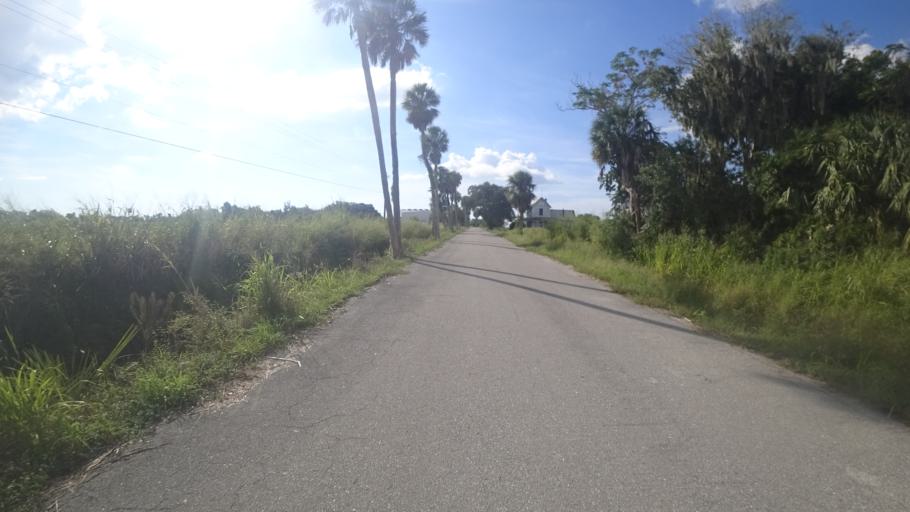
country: US
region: Florida
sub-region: Manatee County
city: Memphis
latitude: 27.5432
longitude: -82.5781
